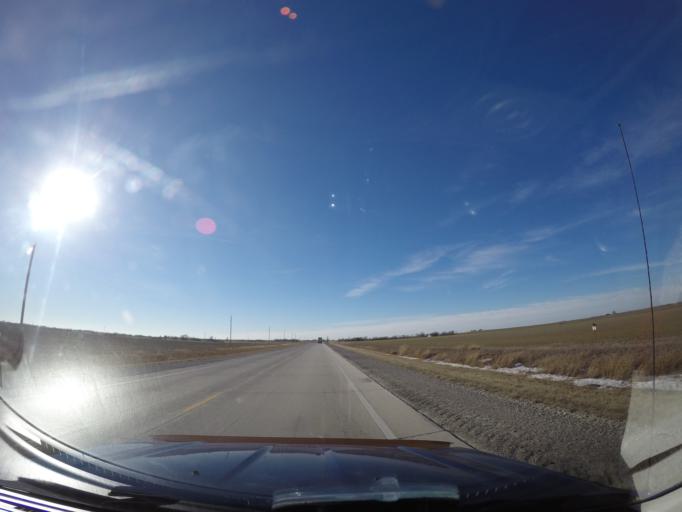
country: US
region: Kansas
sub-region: Marion County
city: Hillsboro
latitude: 38.3626
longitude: -97.1470
